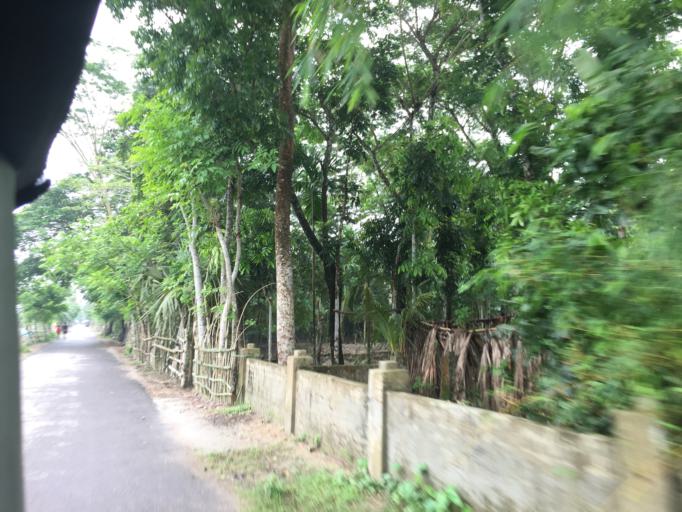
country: BD
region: Barisal
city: Mathba
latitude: 22.2094
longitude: 89.9349
